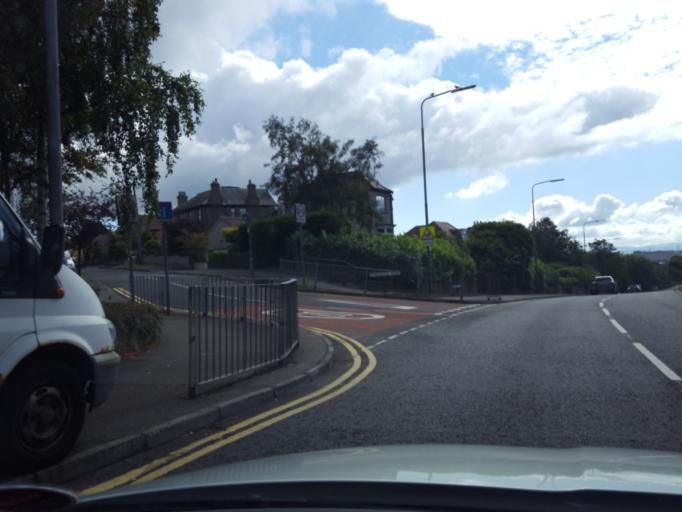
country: GB
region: Scotland
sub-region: Fife
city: Dunfermline
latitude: 56.0608
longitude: -3.4439
